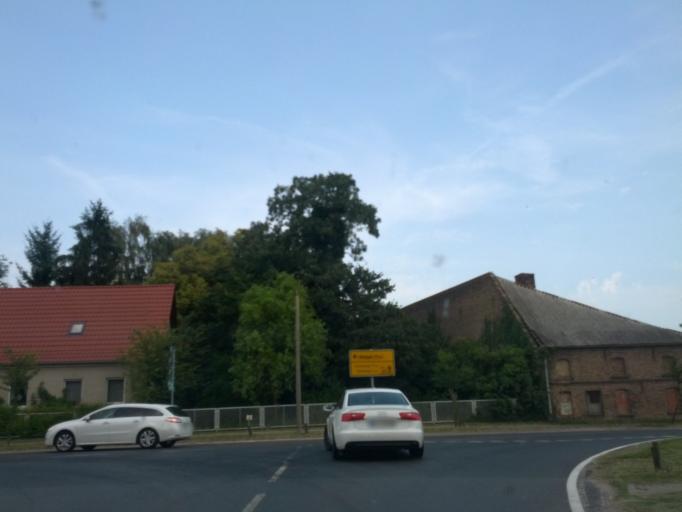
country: DE
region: Brandenburg
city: Kremmen
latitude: 52.7291
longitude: 12.9540
